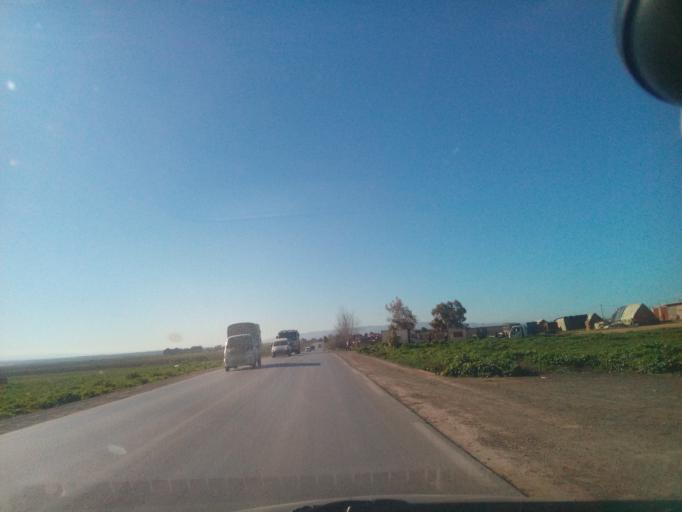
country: DZ
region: Relizane
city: Djidiouia
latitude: 35.8974
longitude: 0.6780
